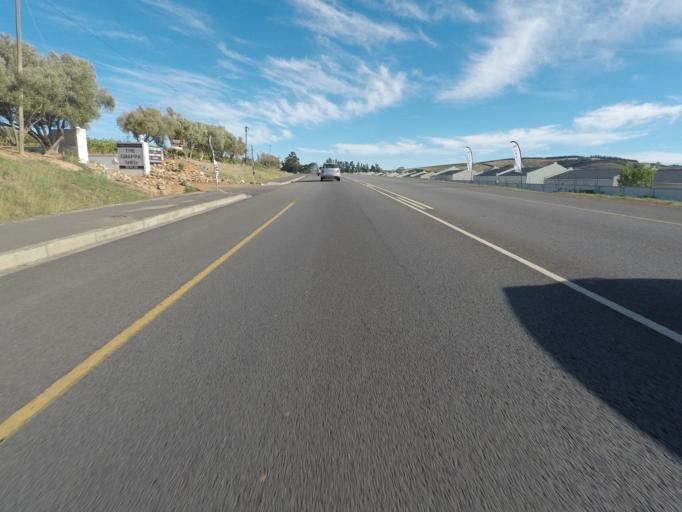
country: ZA
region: Western Cape
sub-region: Cape Winelands District Municipality
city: Stellenbosch
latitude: -33.9092
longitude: 18.8468
